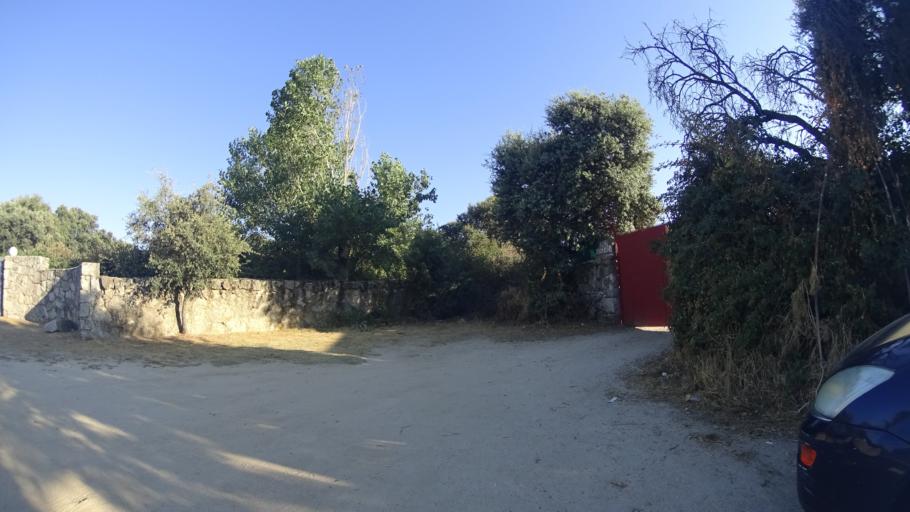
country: ES
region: Madrid
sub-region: Provincia de Madrid
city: Galapagar
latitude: 40.5657
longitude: -3.9914
